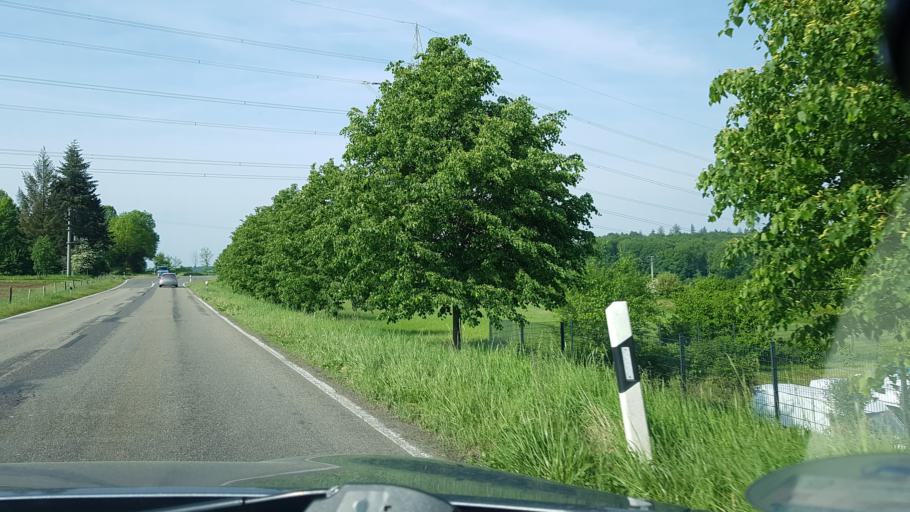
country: DE
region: Rheinland-Pfalz
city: Neuhausel
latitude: 50.3789
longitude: 7.7026
